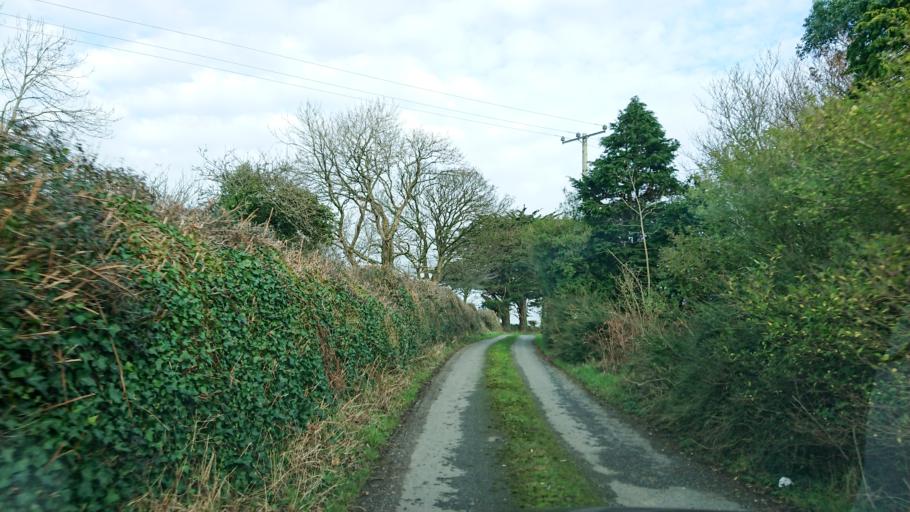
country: IE
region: Munster
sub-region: Waterford
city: Tra Mhor
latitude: 52.1658
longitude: -7.2736
